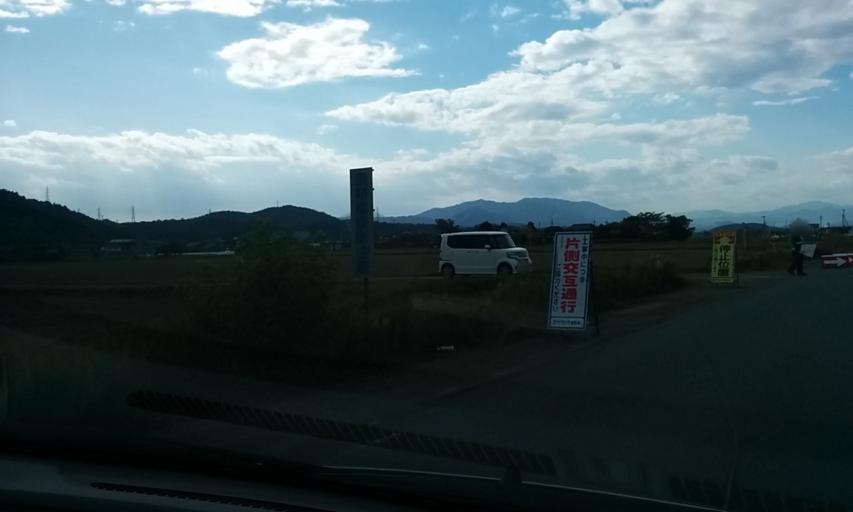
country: JP
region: Kyoto
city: Ayabe
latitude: 35.3070
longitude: 135.1872
